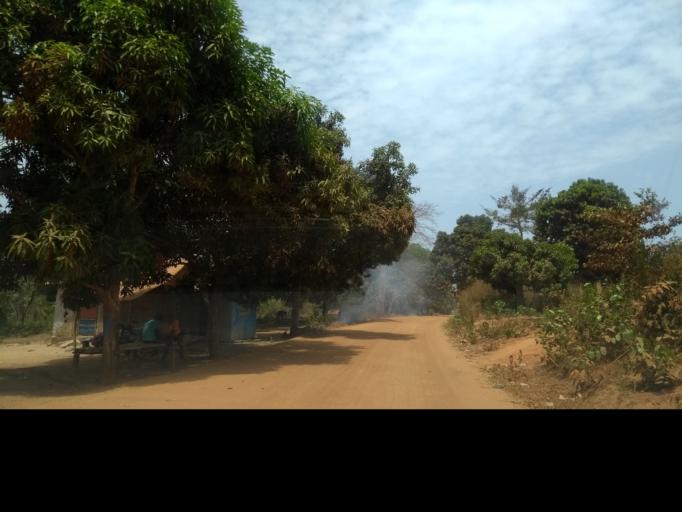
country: GN
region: Kindia
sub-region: Prefecture de Dubreka
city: Dubreka
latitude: 9.7876
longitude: -13.5355
